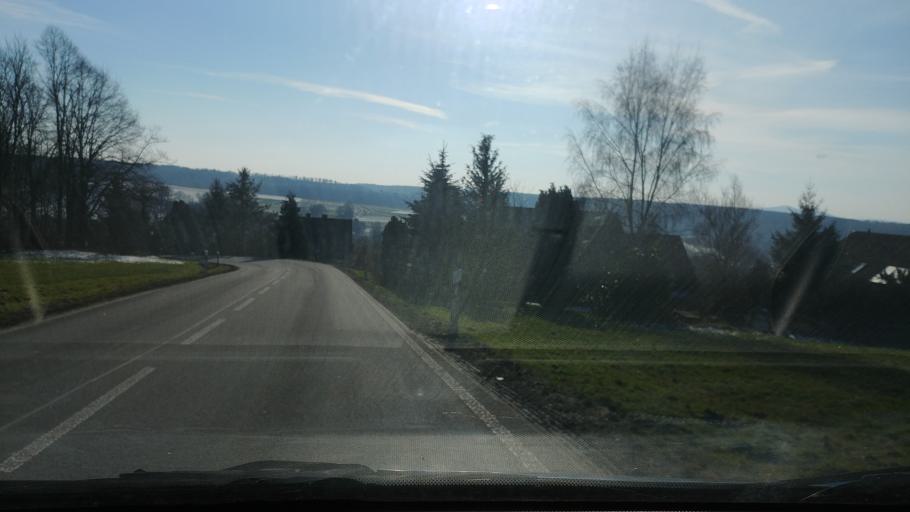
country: DE
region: Lower Saxony
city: Bodenfelde
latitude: 51.5838
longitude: 9.5067
